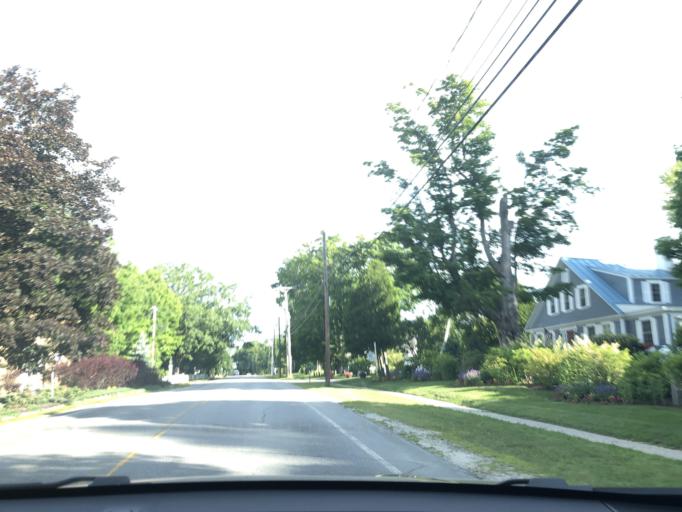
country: US
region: New Hampshire
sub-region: Merrimack County
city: New London
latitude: 43.4092
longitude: -71.9748
